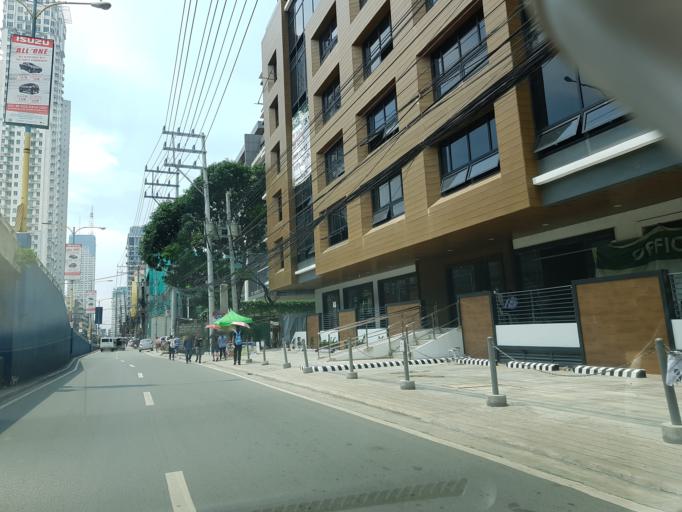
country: PH
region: Metro Manila
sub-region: Pasig
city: Pasig City
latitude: 14.5826
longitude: 121.0521
